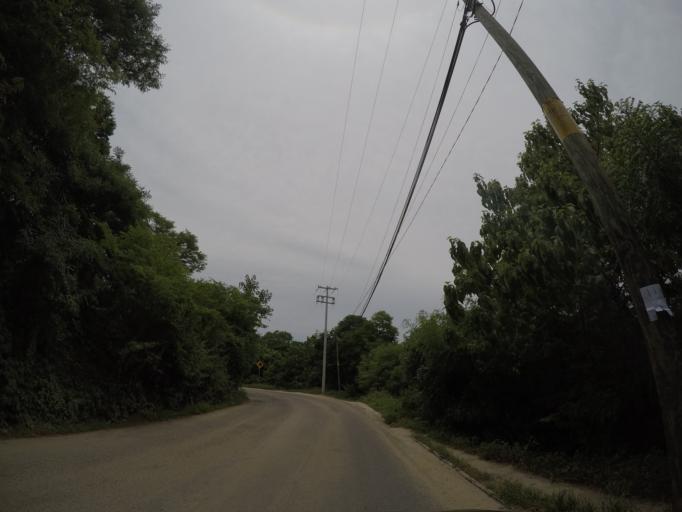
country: MX
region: Oaxaca
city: San Pedro Pochutla
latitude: 15.6671
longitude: -96.4981
